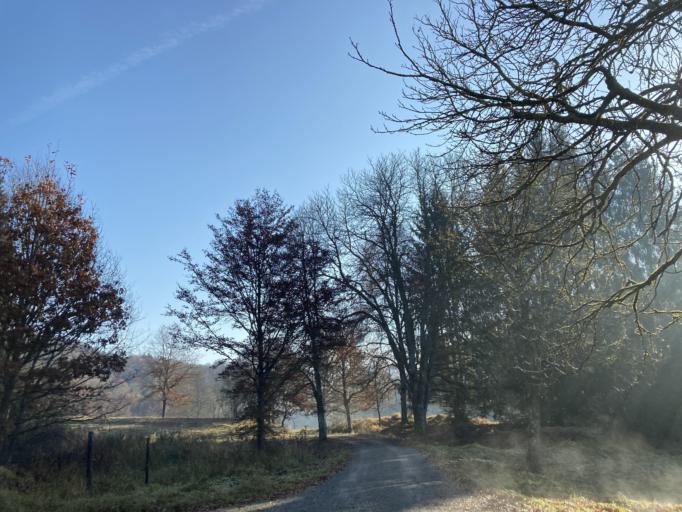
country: DE
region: Baden-Wuerttemberg
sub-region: Regierungsbezirk Stuttgart
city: Hildrizhausen
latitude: 48.5875
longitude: 8.9828
